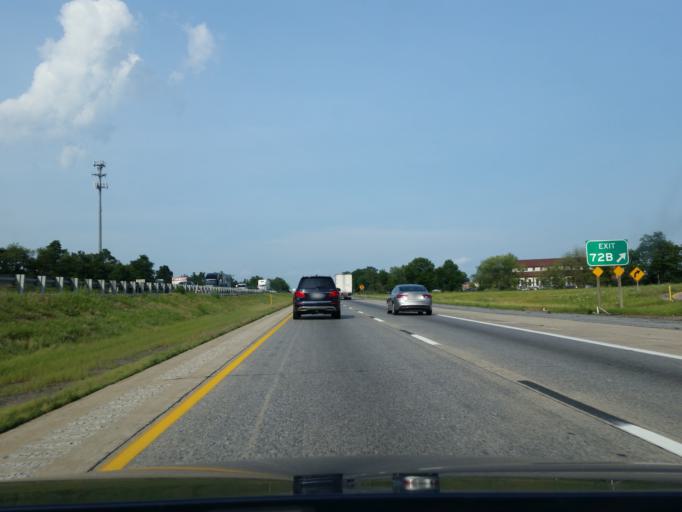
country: US
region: Pennsylvania
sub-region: Dauphin County
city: Linglestown
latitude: 40.3261
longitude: -76.7903
